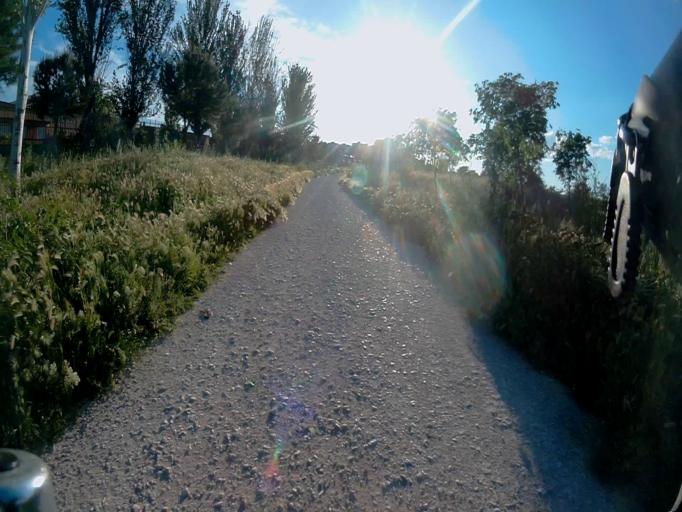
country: ES
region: Madrid
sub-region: Provincia de Madrid
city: Fuenlabrada
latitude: 40.2977
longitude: -3.7959
